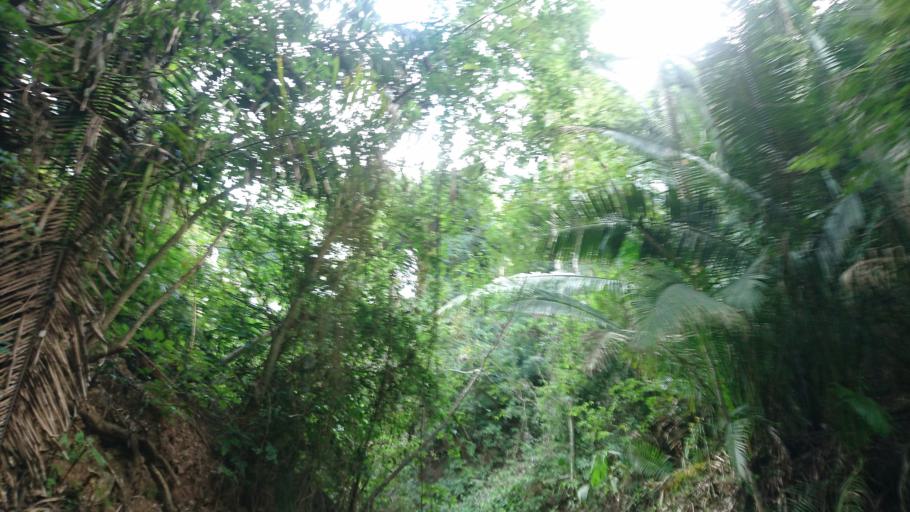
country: MX
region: Nayarit
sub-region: Bahia de Banderas
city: Corral del Risco (Punta de Mita)
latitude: 20.8277
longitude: -105.4623
